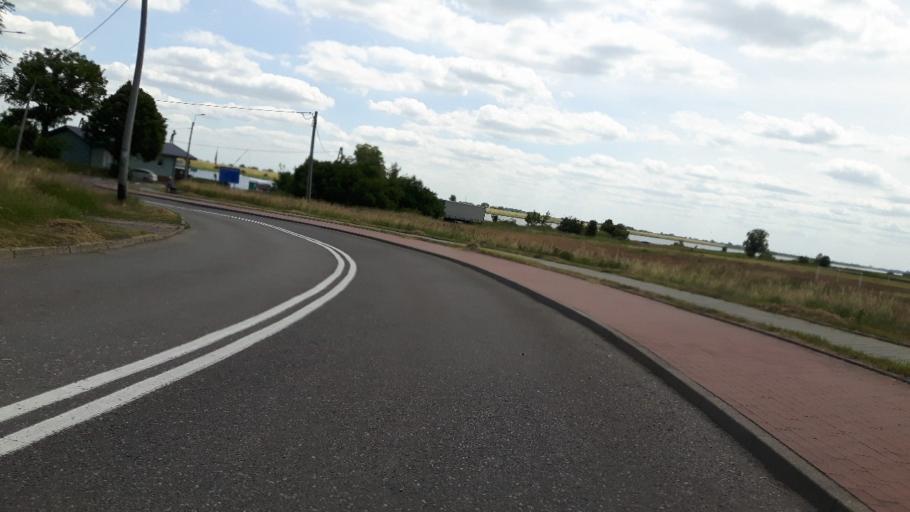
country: PL
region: Pomeranian Voivodeship
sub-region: Powiat nowodworski
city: Ostaszewo
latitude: 54.3341
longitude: 18.9353
